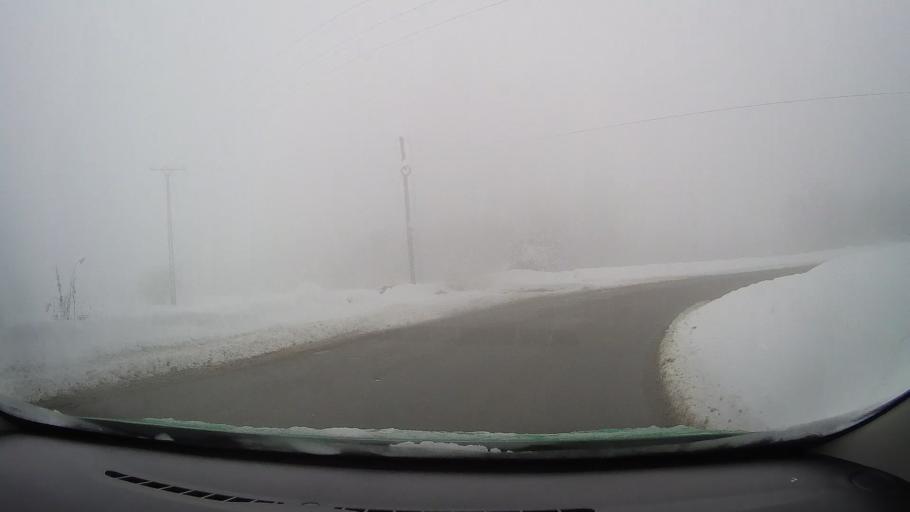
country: RO
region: Sibiu
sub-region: Comuna Poiana Sibiului
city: Poiana Sibiului
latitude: 45.8073
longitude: 23.7544
